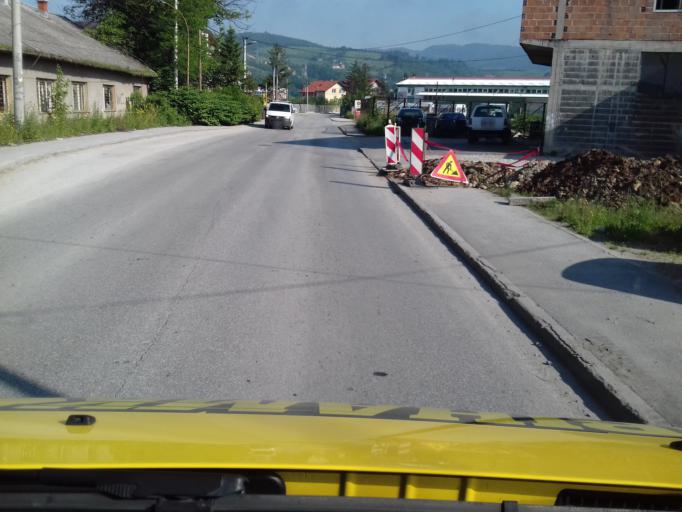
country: BA
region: Federation of Bosnia and Herzegovina
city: Vogosca
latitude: 43.8753
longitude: 18.3096
